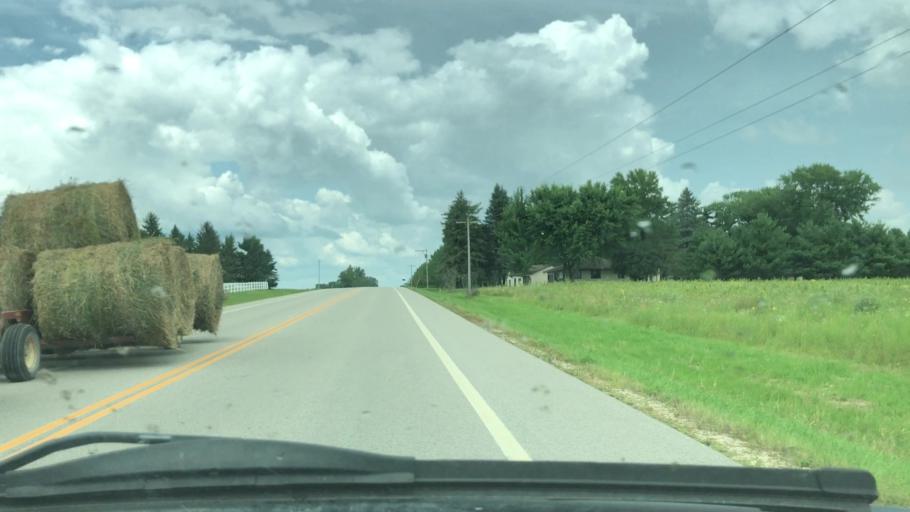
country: US
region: Minnesota
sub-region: Olmsted County
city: Stewartville
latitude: 43.8650
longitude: -92.5287
